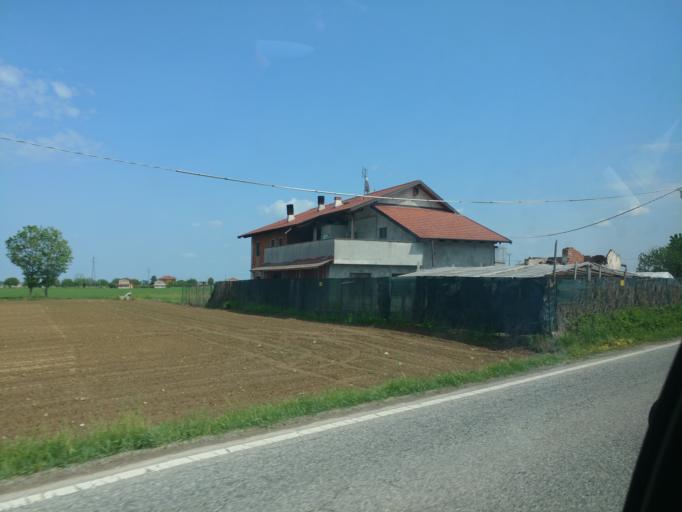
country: IT
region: Piedmont
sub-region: Provincia di Torino
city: Cavour
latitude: 44.7549
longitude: 7.4034
